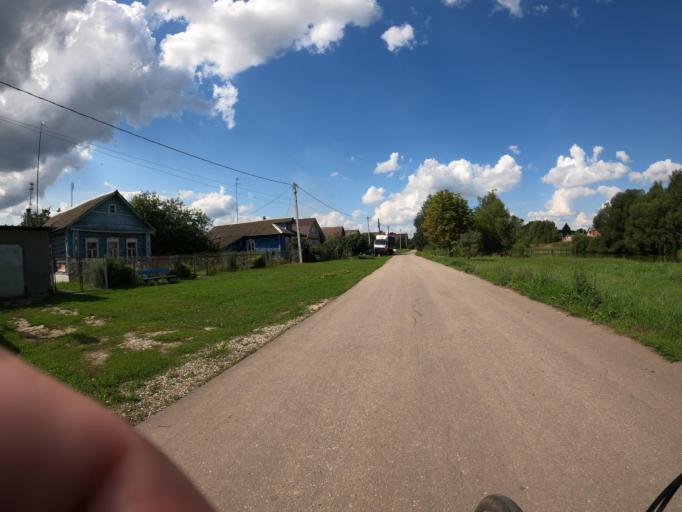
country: RU
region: Moskovskaya
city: Voskresensk
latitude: 55.2688
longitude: 38.6560
